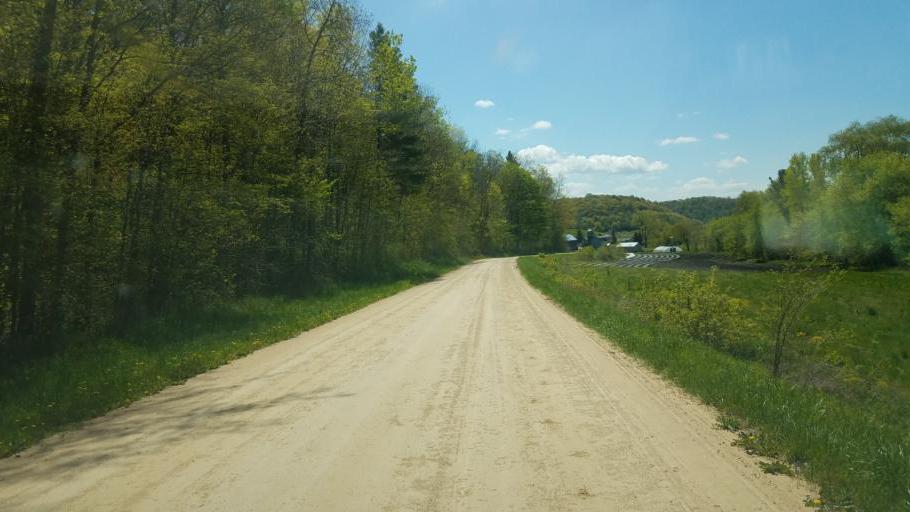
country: US
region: Wisconsin
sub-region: Vernon County
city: Hillsboro
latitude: 43.5927
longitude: -90.4099
